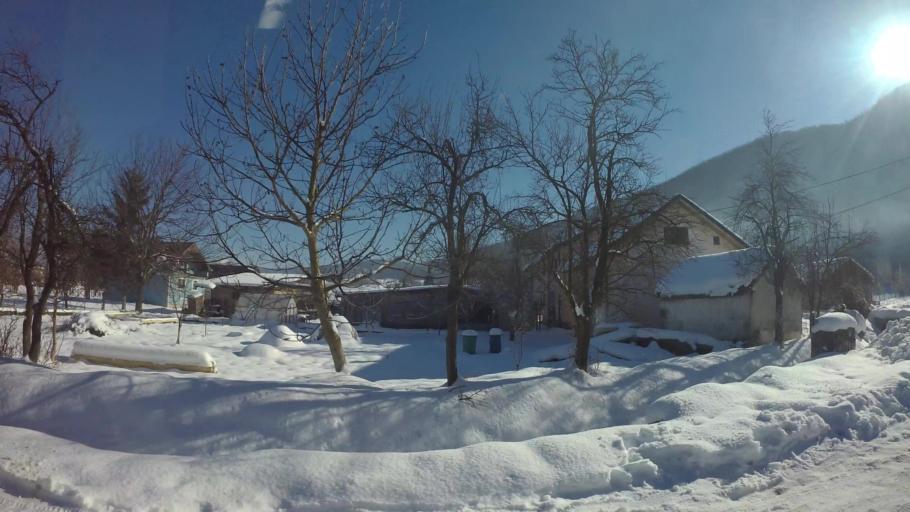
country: BA
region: Federation of Bosnia and Herzegovina
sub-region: Kanton Sarajevo
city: Sarajevo
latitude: 43.7890
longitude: 18.3374
